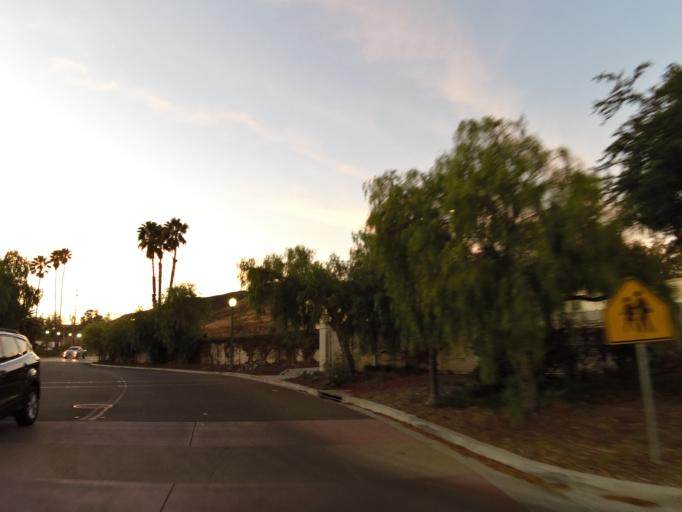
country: US
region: California
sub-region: Ventura County
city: Casa Conejo
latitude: 34.1926
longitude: -118.9365
